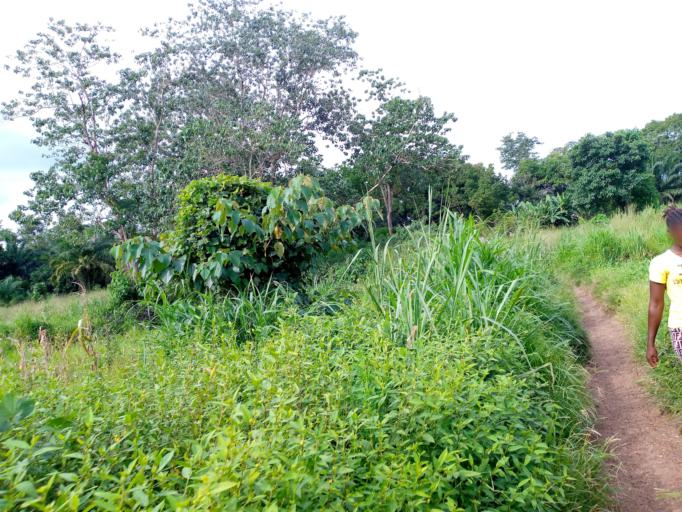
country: SL
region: Northern Province
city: Magburaka
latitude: 8.7178
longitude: -11.9466
